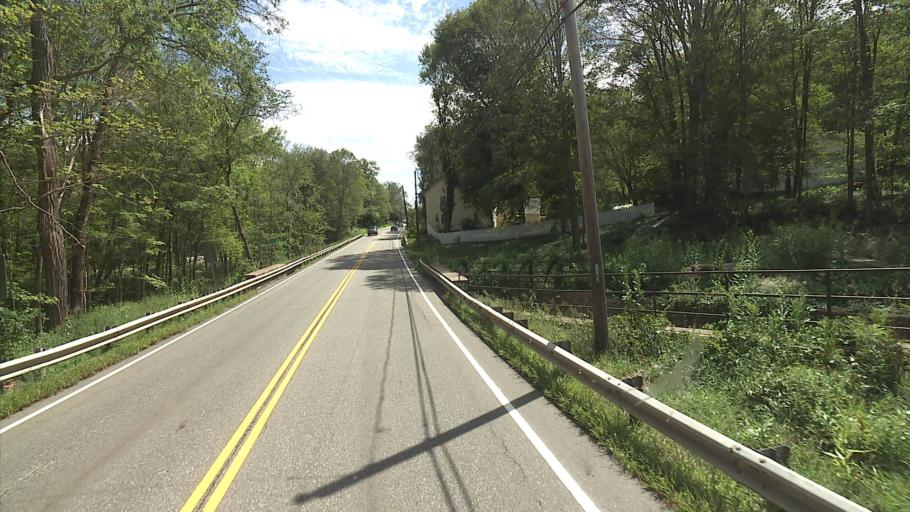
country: US
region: Connecticut
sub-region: Tolland County
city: Mansfield City
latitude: 41.7685
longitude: -72.2009
